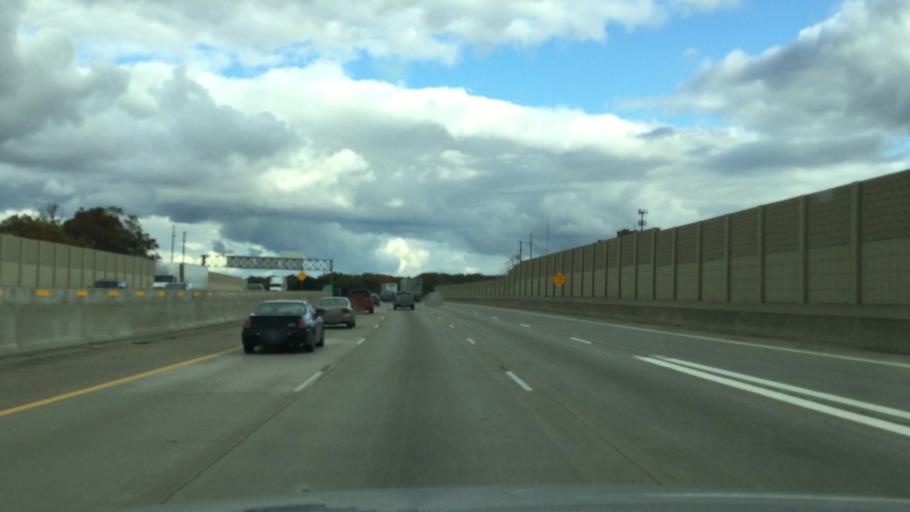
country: US
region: Michigan
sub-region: Kalamazoo County
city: Portage
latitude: 42.2367
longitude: -85.5836
